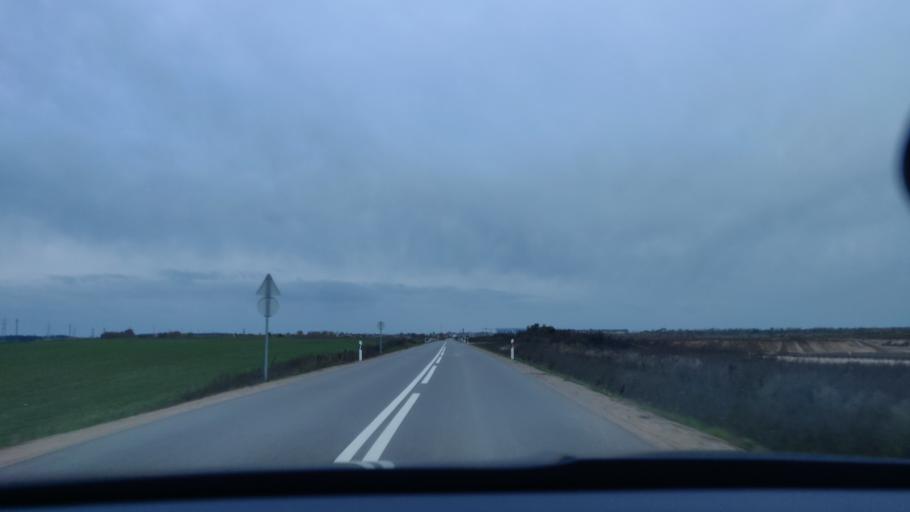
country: LT
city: Lentvaris
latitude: 54.6019
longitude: 25.0079
